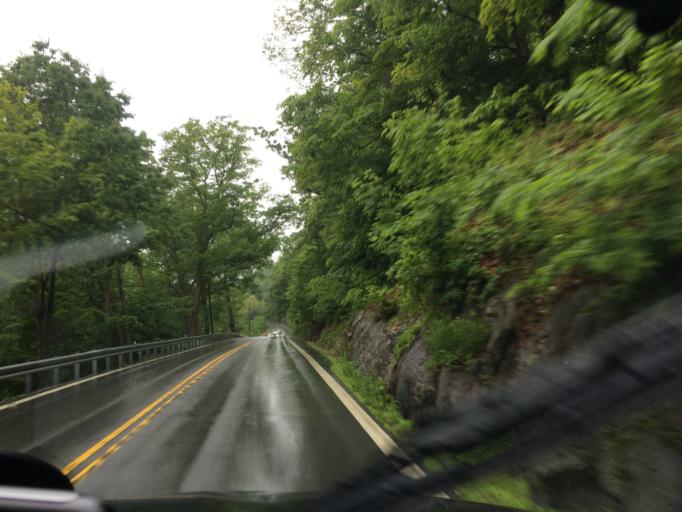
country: US
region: Maryland
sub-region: Frederick County
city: Thurmont
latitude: 39.6642
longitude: -77.4496
